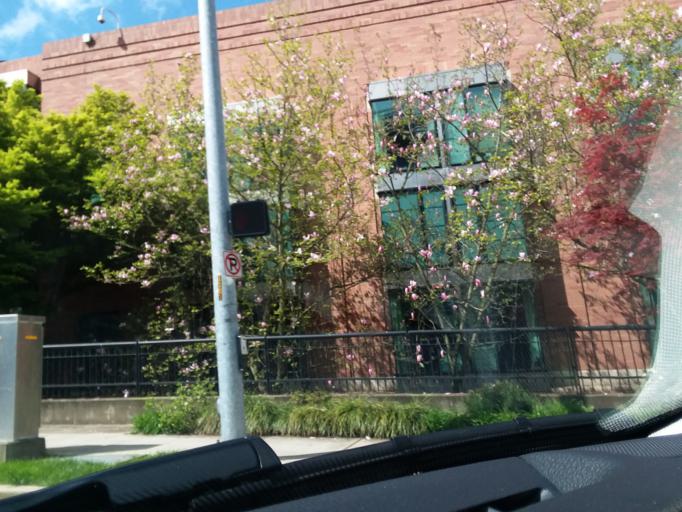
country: US
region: Washington
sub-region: King County
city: Seattle
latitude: 47.6289
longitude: -122.3293
